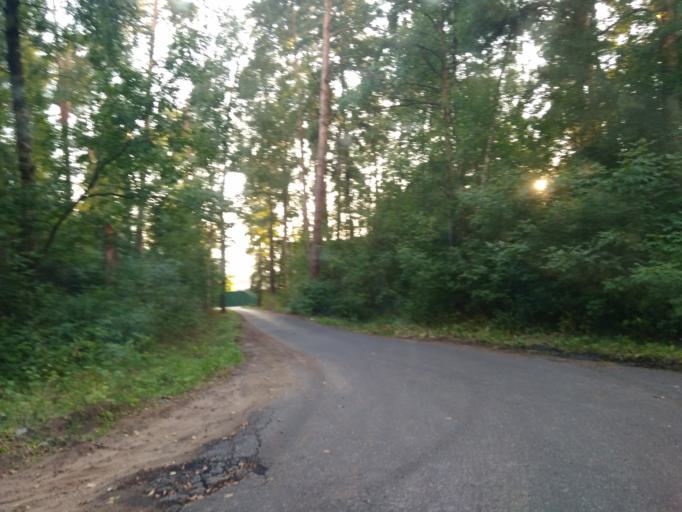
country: RU
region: Moskovskaya
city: Zhukovskiy
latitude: 55.5803
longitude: 38.1143
